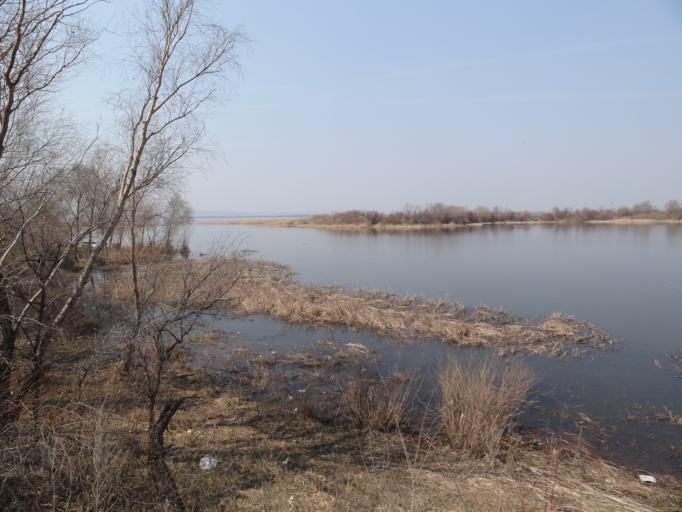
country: RU
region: Saratov
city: Privolzhskiy
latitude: 51.2913
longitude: 45.9540
